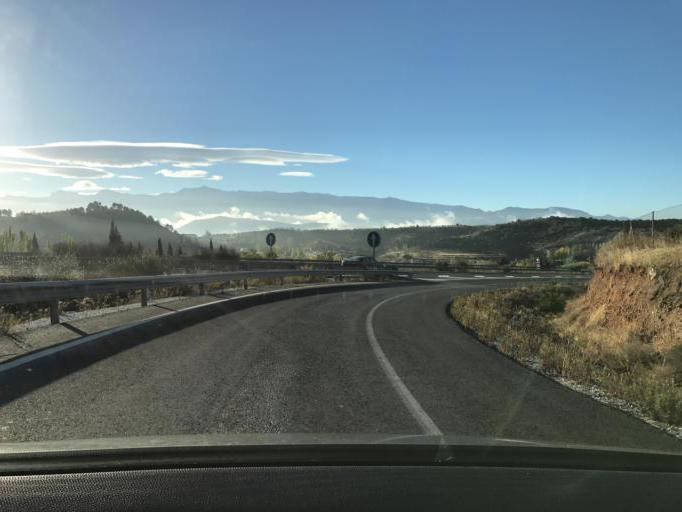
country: ES
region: Andalusia
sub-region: Provincia de Granada
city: Huetor Santillan
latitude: 37.2355
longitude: -3.4978
